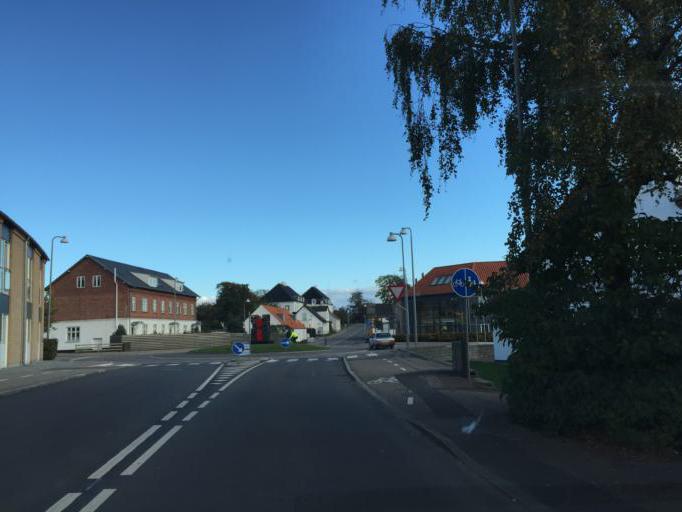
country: DK
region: Zealand
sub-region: Odsherred Kommune
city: Asnaes
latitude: 55.8103
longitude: 11.5025
